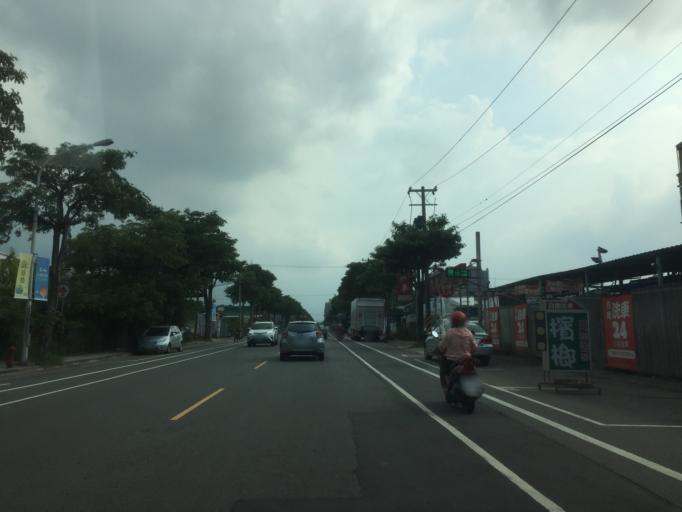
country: TW
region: Taiwan
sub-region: Taoyuan
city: Taoyuan
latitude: 24.9719
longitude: 121.3069
